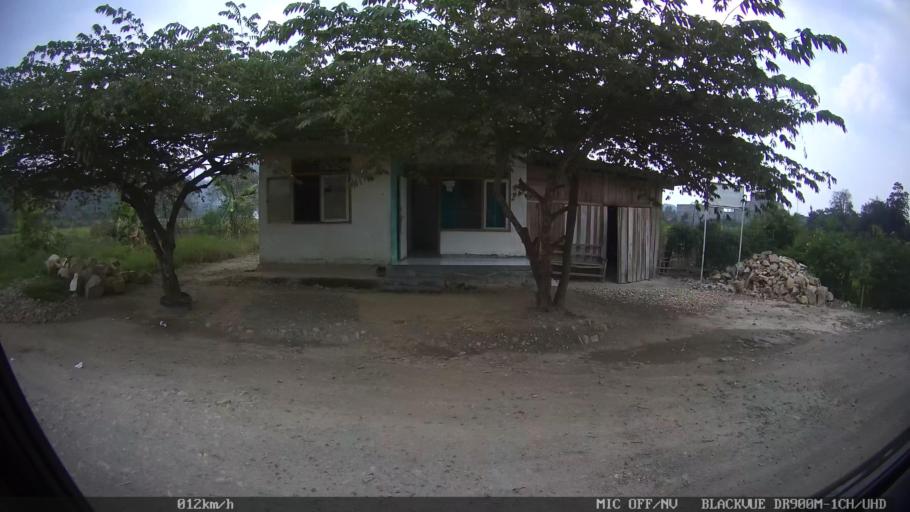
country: ID
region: Lampung
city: Gadingrejo
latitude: -5.3809
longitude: 105.0345
